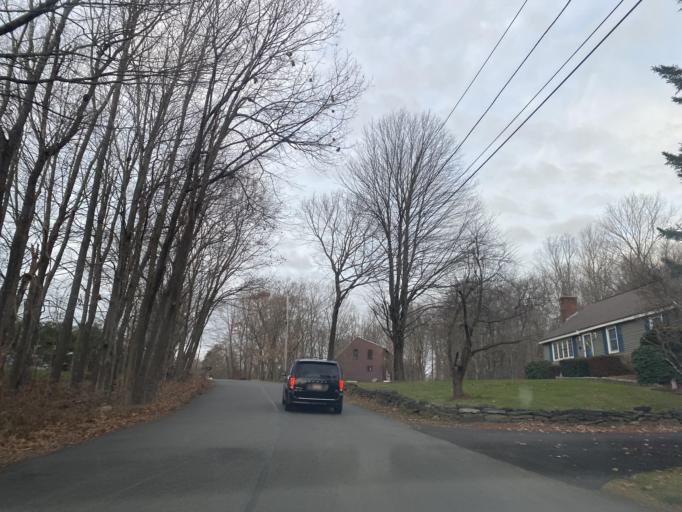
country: US
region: Massachusetts
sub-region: Worcester County
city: Paxton
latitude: 42.2760
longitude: -71.9327
